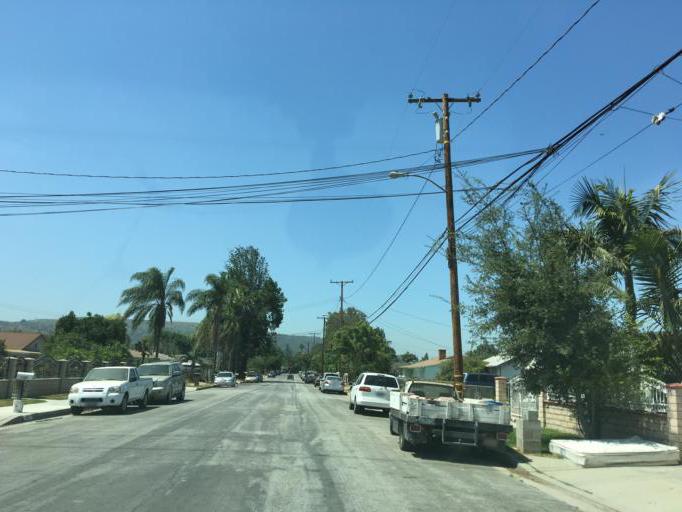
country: US
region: California
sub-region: Los Angeles County
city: Avocado Heights
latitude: 34.0476
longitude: -117.9951
